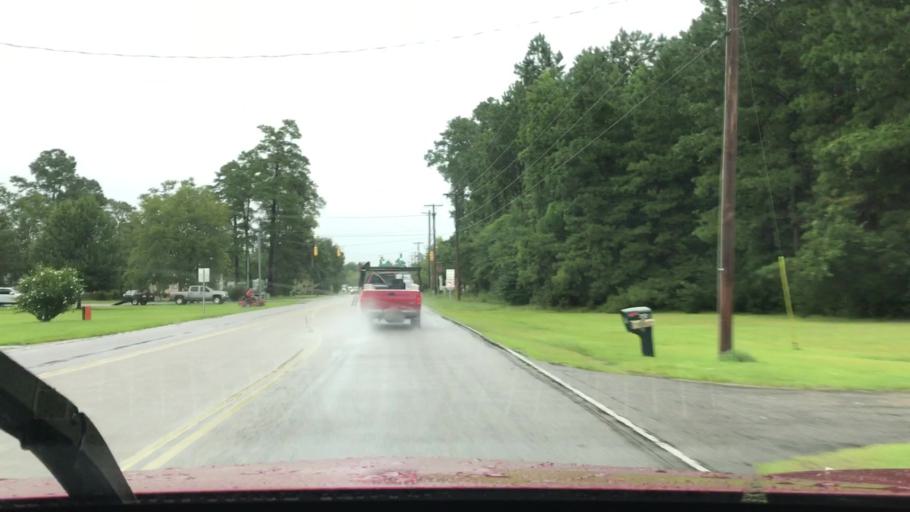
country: US
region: South Carolina
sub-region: Horry County
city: Conway
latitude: 33.8446
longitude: -79.0267
